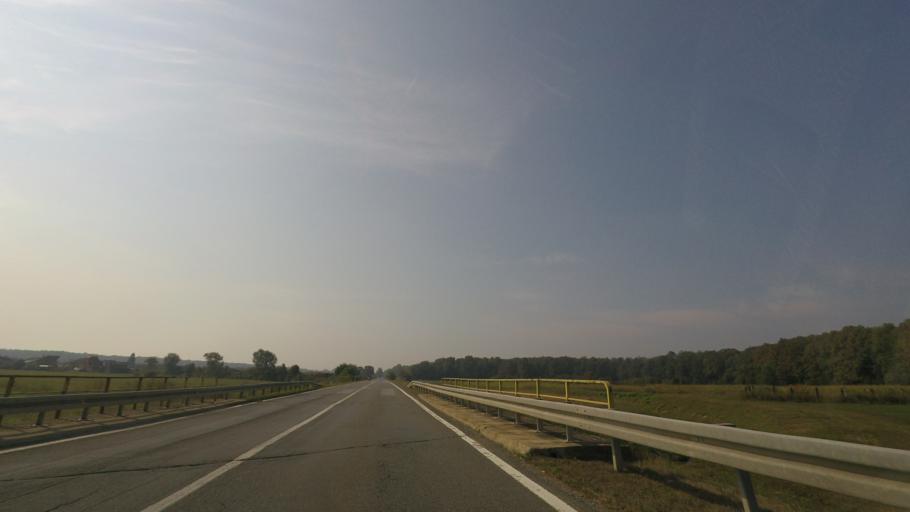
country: HR
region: Sisacko-Moslavacka
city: Novska
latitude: 45.3161
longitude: 16.9492
